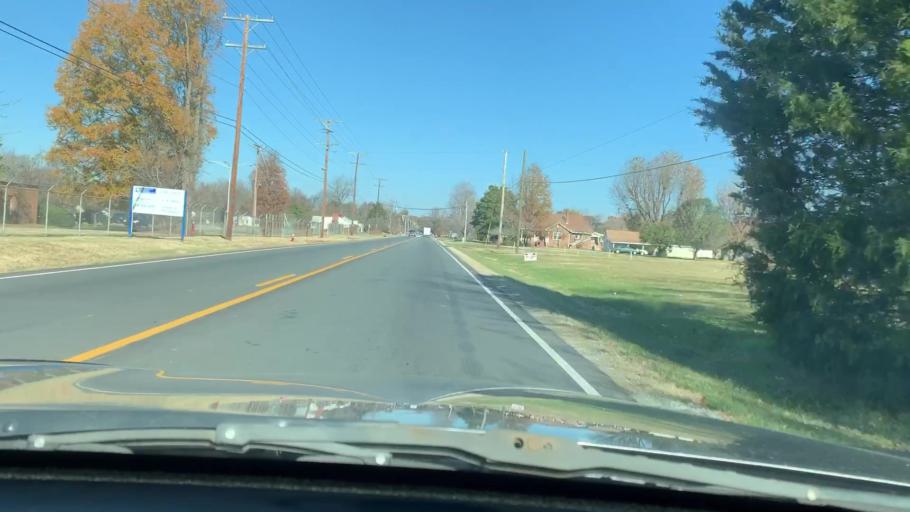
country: US
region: North Carolina
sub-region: Alamance County
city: Haw River
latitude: 36.0832
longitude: -79.3480
